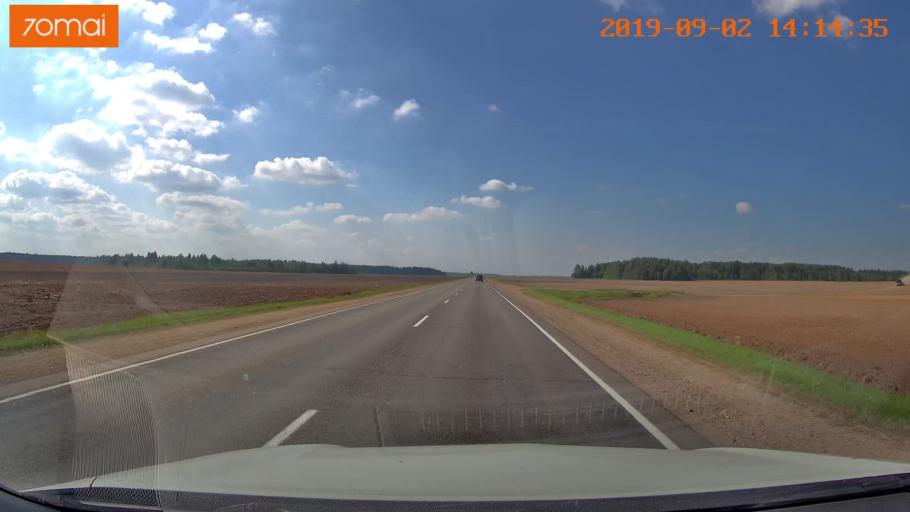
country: BY
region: Mogilev
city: Chavusy
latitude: 53.8075
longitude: 30.8783
